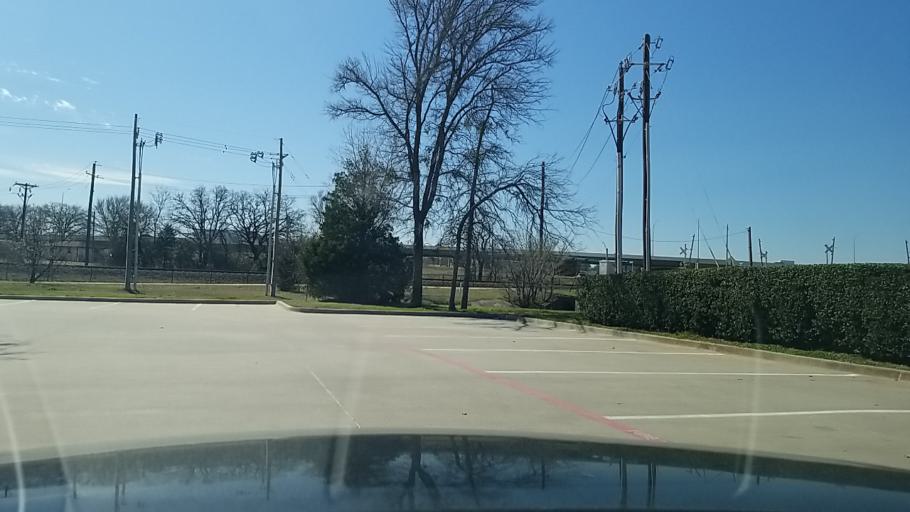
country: US
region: Texas
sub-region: Denton County
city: Corinth
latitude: 33.1523
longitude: -97.0579
